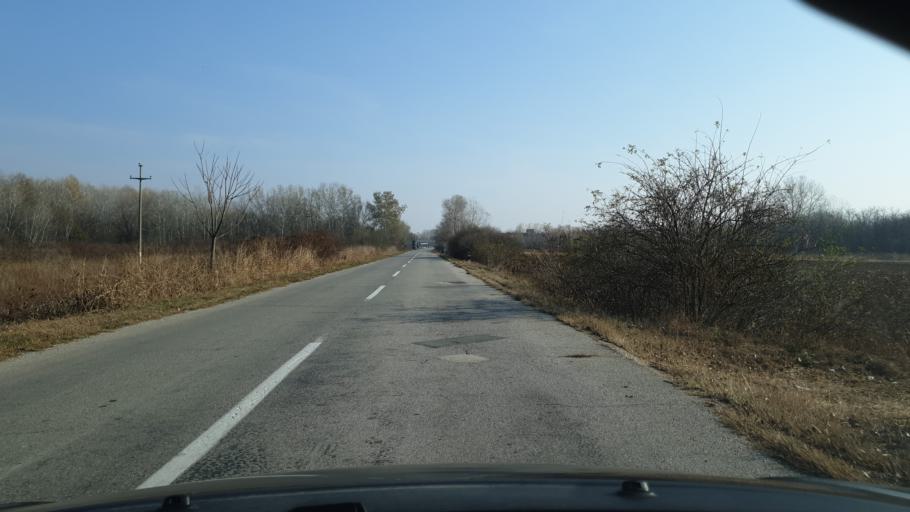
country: BG
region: Vidin
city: Bregovo
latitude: 44.1562
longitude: 22.6166
